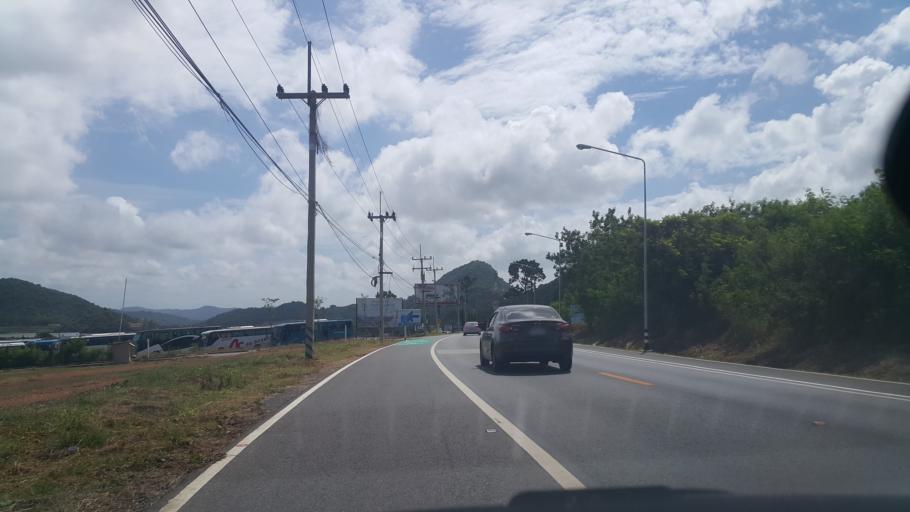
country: TH
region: Rayong
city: Ban Chang
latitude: 12.7595
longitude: 100.9674
